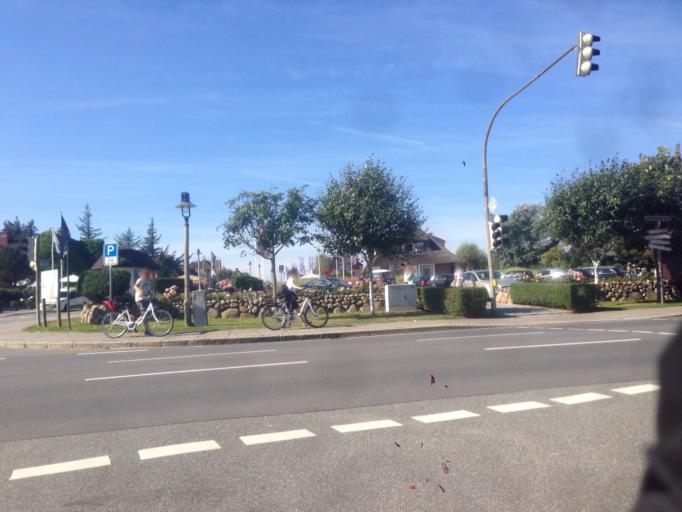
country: DE
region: Schleswig-Holstein
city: Tinnum
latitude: 54.9556
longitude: 8.3424
